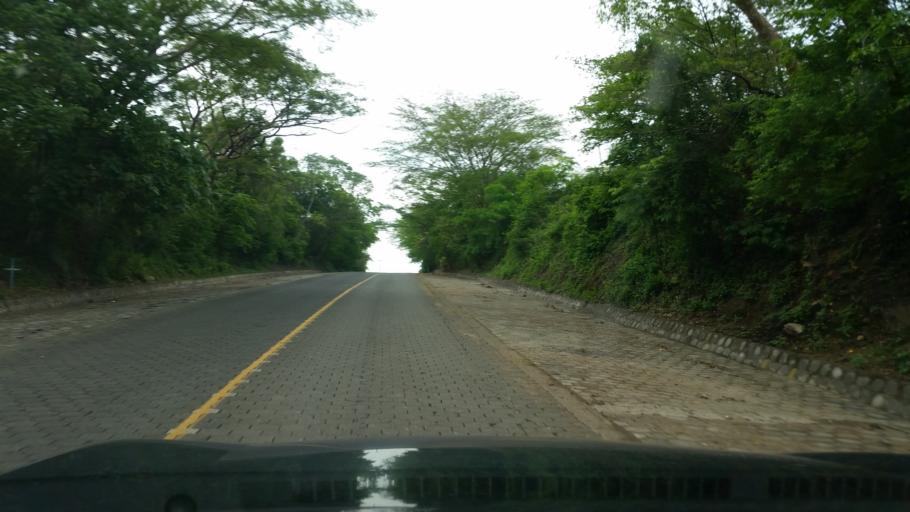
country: NI
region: Managua
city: Carlos Fonseca Amador
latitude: 11.9032
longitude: -86.5105
